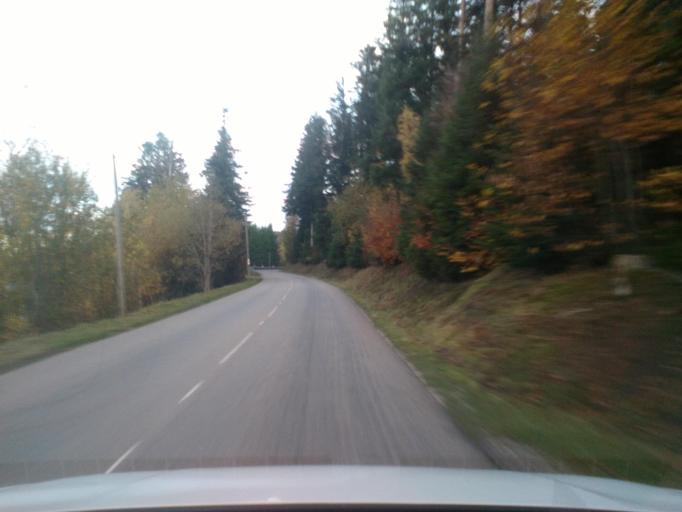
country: FR
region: Lorraine
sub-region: Departement des Vosges
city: Fraize
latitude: 48.1985
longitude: 7.0145
